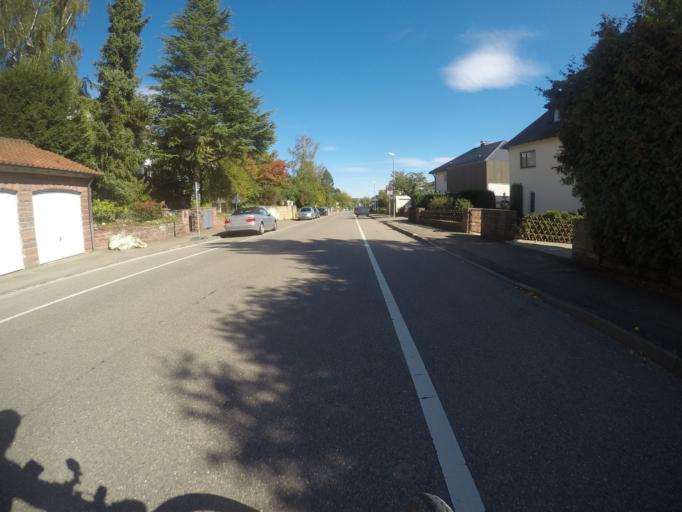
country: DE
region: Baden-Wuerttemberg
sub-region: Regierungsbezirk Stuttgart
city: Stuttgart-Ost
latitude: 48.7613
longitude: 9.2178
